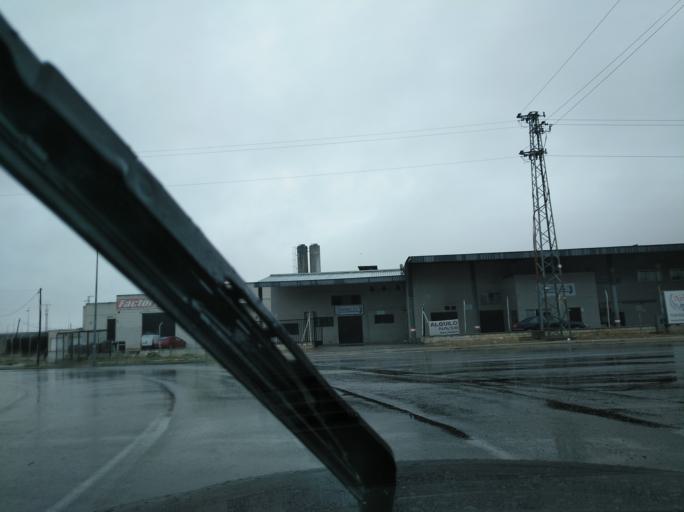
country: ES
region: Extremadura
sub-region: Provincia de Badajoz
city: Badajoz
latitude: 38.8959
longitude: -6.9877
